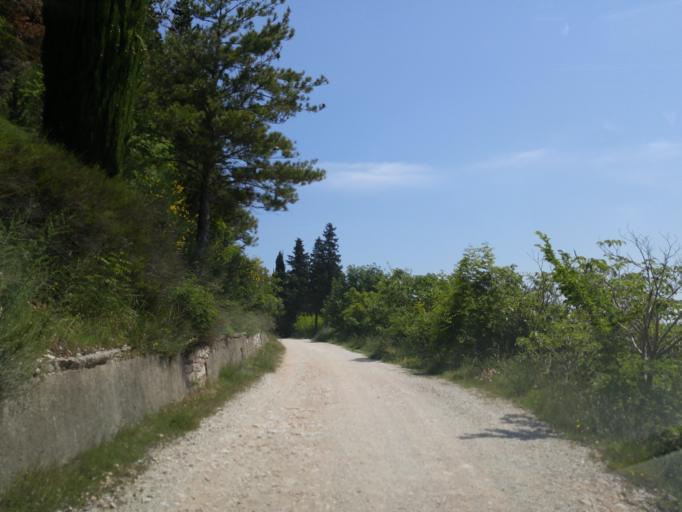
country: IT
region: The Marches
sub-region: Provincia di Pesaro e Urbino
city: Fossombrone
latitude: 43.6898
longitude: 12.8048
